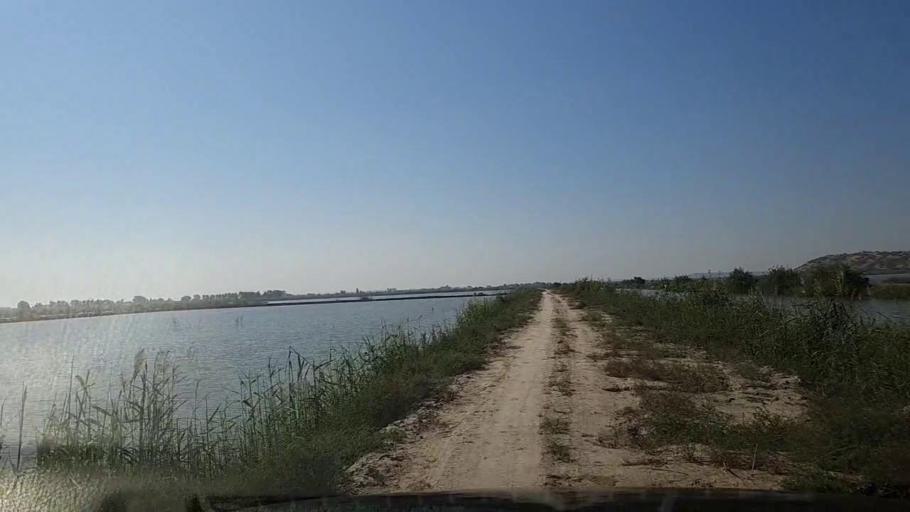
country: PK
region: Sindh
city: Thatta
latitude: 24.6796
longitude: 67.8903
